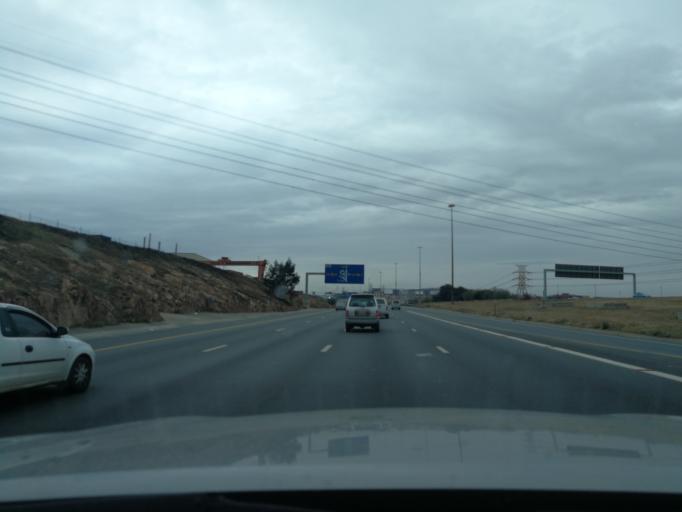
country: ZA
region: Gauteng
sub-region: Ekurhuleni Metropolitan Municipality
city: Germiston
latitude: -26.2404
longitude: 28.1292
